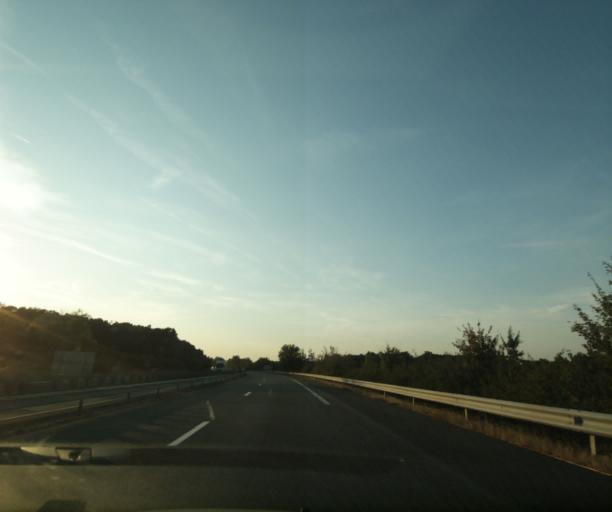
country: FR
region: Aquitaine
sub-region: Departement du Lot-et-Garonne
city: Boe
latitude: 44.1585
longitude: 0.6157
